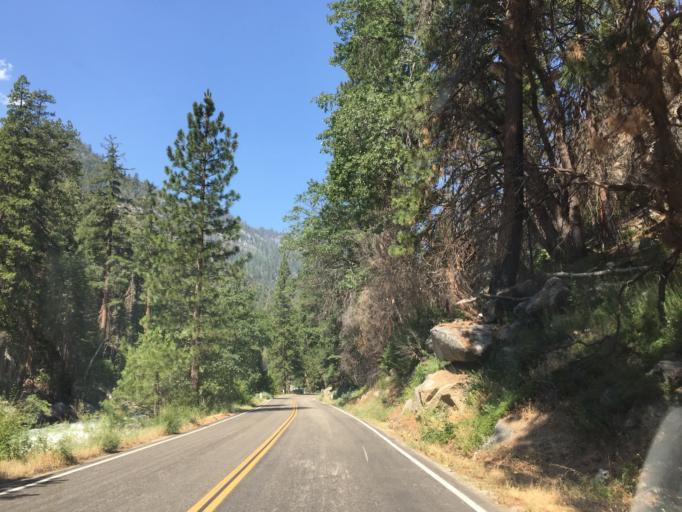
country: US
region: California
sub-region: Tulare County
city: Three Rivers
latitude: 36.8034
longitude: -118.7286
